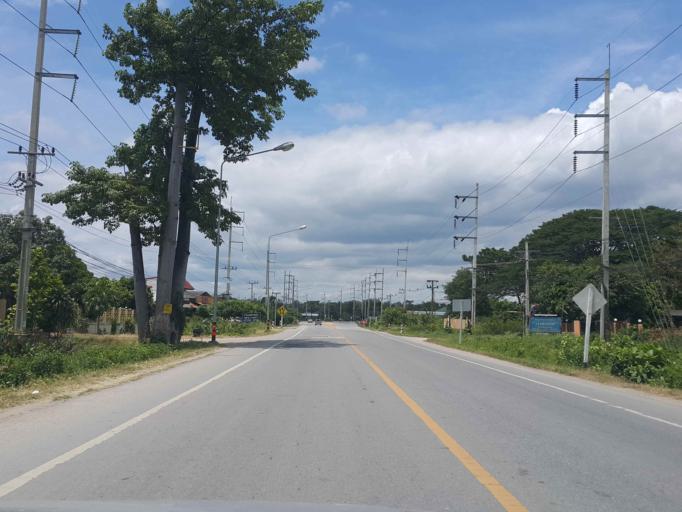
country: TH
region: Lamphun
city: Ban Hong
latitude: 18.3384
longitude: 98.8165
